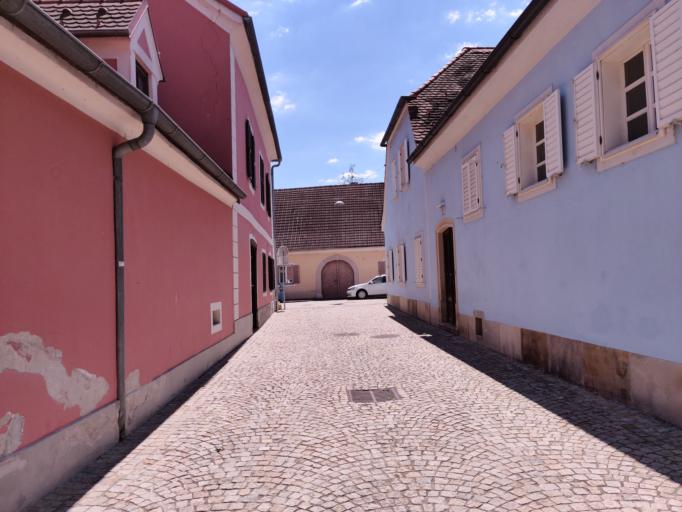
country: AT
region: Styria
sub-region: Politischer Bezirk Suedoststeiermark
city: Bad Radkersburg
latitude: 46.6868
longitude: 15.9876
